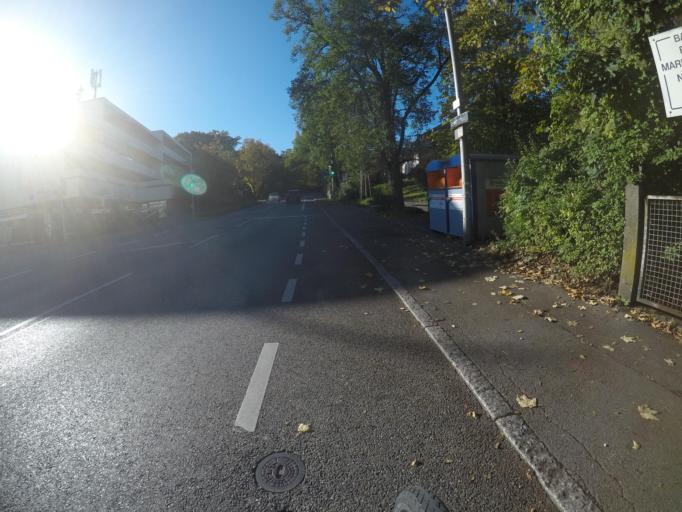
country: DE
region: Baden-Wuerttemberg
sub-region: Regierungsbezirk Stuttgart
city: Steinenbronn
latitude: 48.7172
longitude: 9.1059
